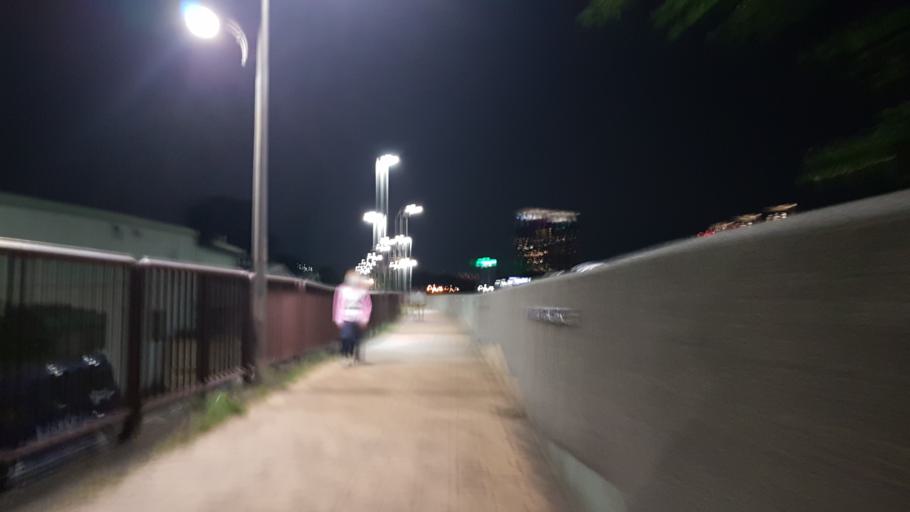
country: TW
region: Taipei
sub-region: Taipei
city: Banqiao
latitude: 24.9632
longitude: 121.5337
